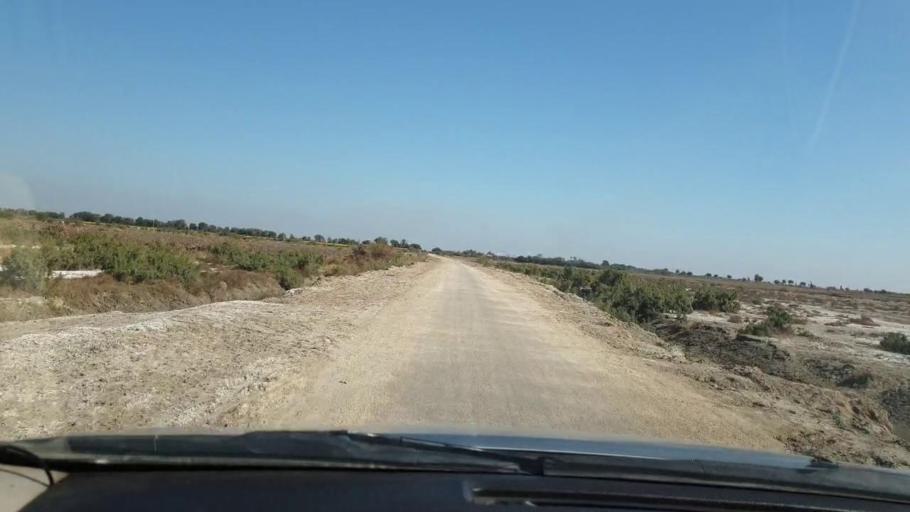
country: PK
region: Sindh
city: Berani
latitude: 25.7734
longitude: 68.9549
